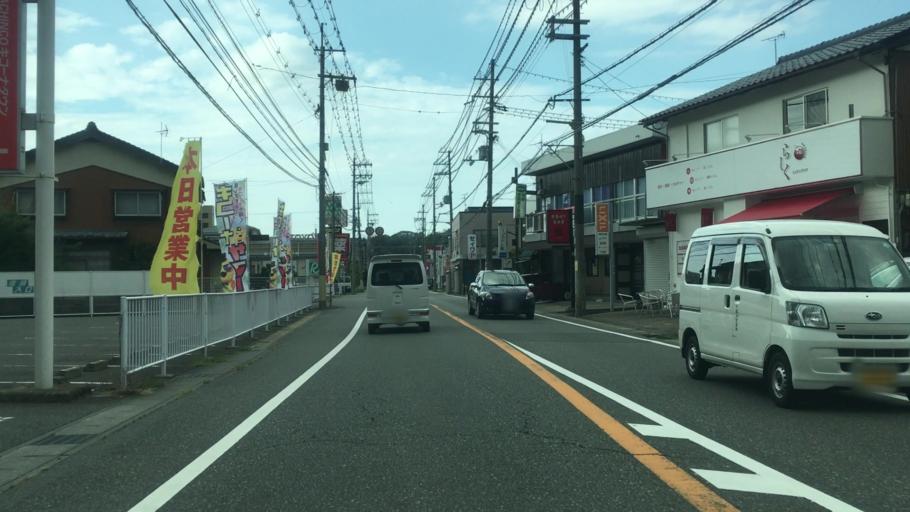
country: JP
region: Hyogo
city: Toyooka
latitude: 35.5318
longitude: 134.8197
